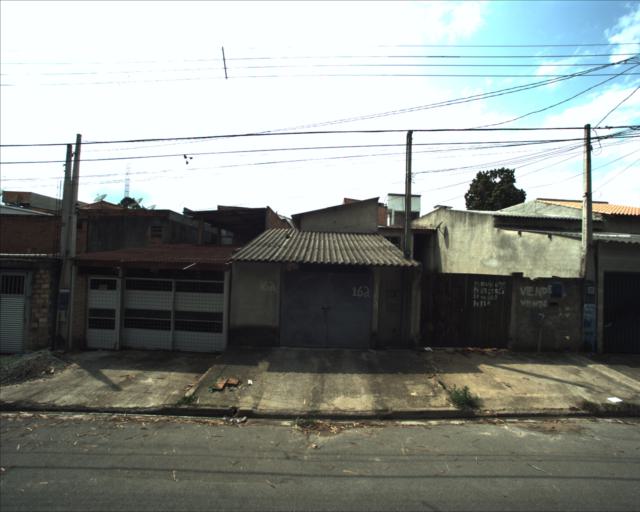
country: BR
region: Sao Paulo
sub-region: Sorocaba
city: Sorocaba
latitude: -23.4320
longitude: -47.5131
